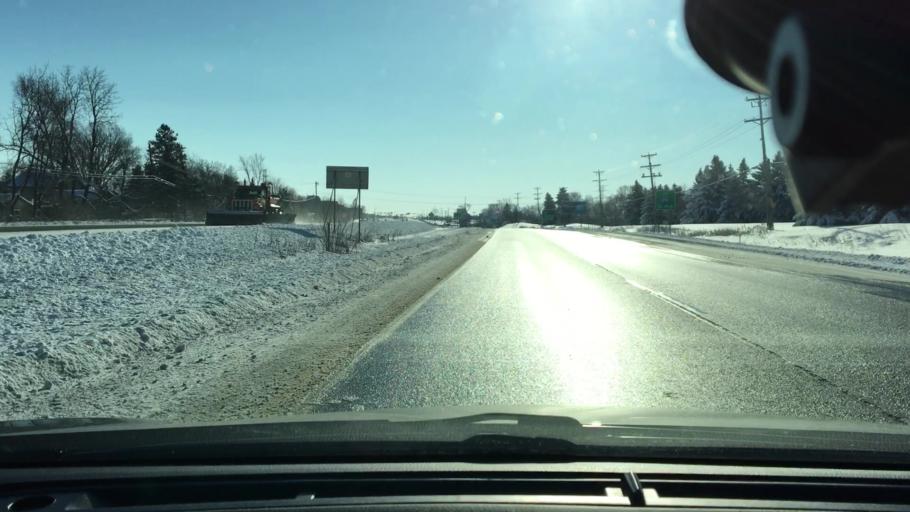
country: US
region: Minnesota
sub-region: Hennepin County
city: Plymouth
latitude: 45.0144
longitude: -93.4692
